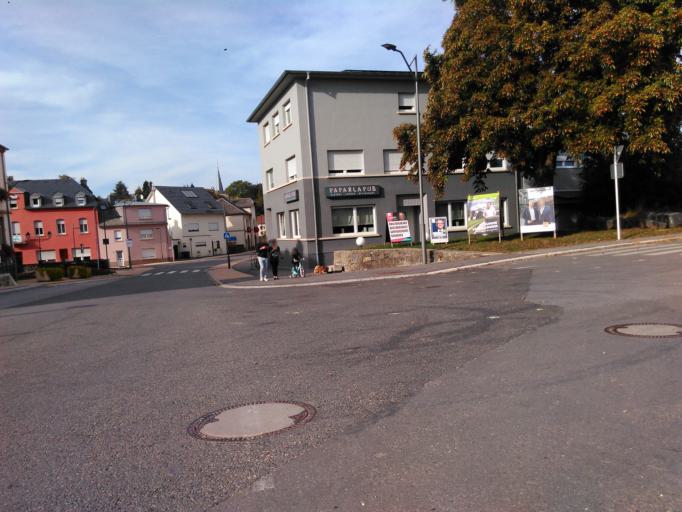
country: LU
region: Luxembourg
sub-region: Canton de Capellen
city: Steinfort
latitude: 49.6440
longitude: 5.9156
